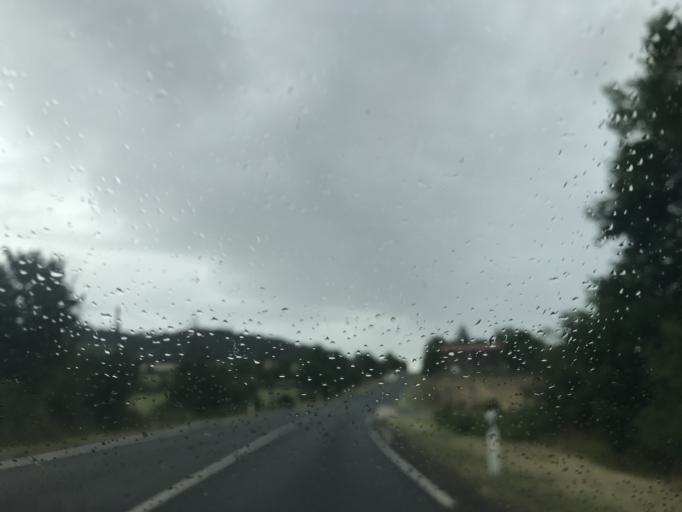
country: FR
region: Auvergne
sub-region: Departement de la Haute-Loire
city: Polignac
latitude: 45.0836
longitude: 3.8195
